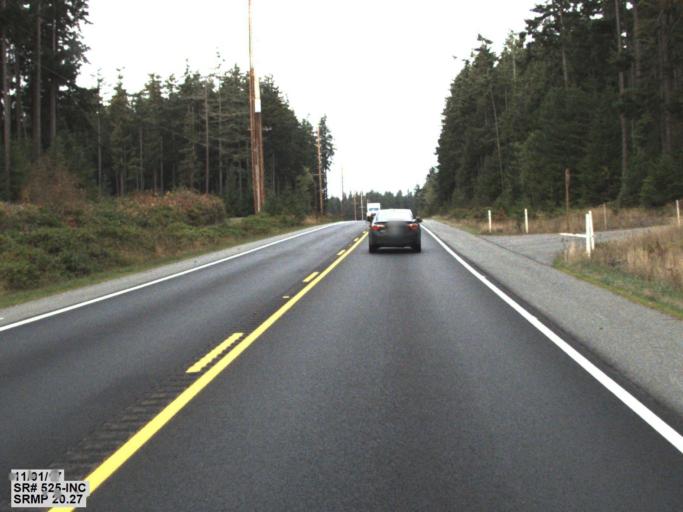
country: US
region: Washington
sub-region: Island County
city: Freeland
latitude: 48.0303
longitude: -122.5620
